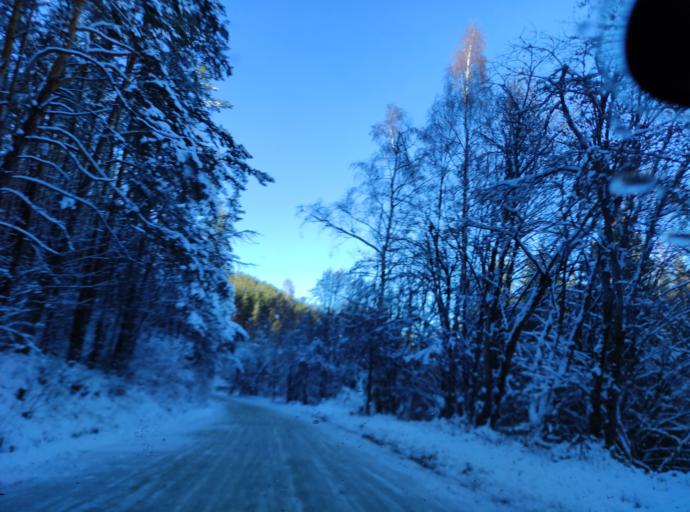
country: BG
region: Sofia-Capital
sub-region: Stolichna Obshtina
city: Sofia
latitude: 42.5986
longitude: 23.3049
